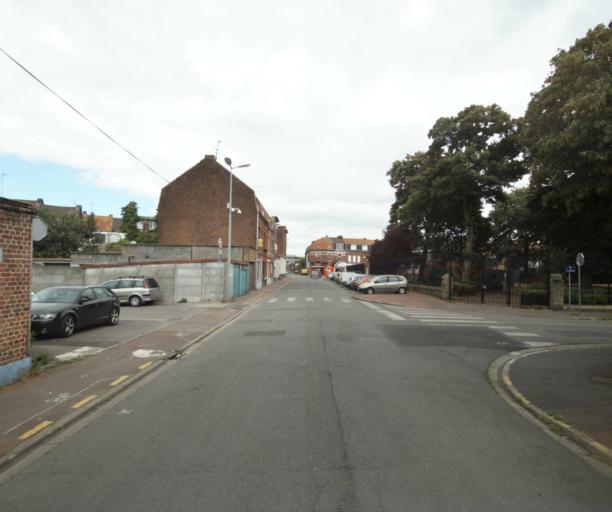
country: FR
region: Nord-Pas-de-Calais
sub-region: Departement du Nord
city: Croix
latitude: 50.6940
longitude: 3.1525
